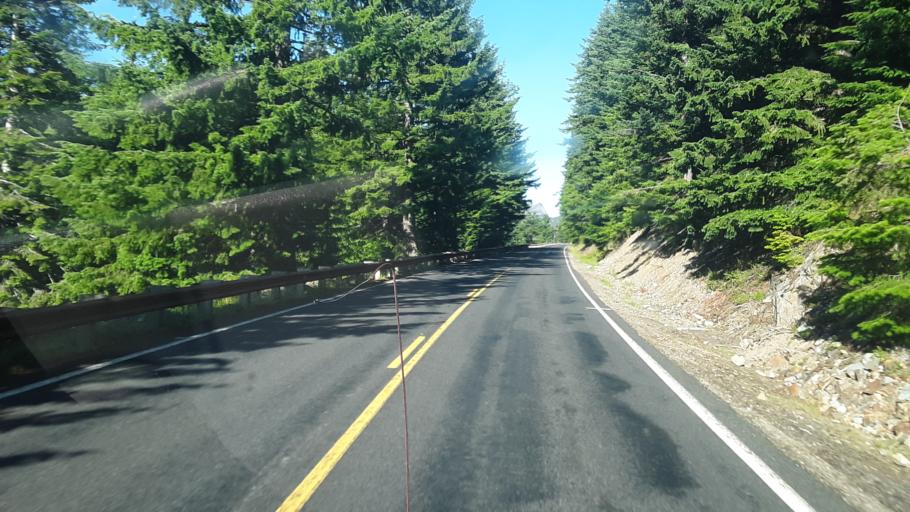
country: US
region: Washington
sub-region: Kittitas County
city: Cle Elum
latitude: 46.8984
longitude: -121.4432
